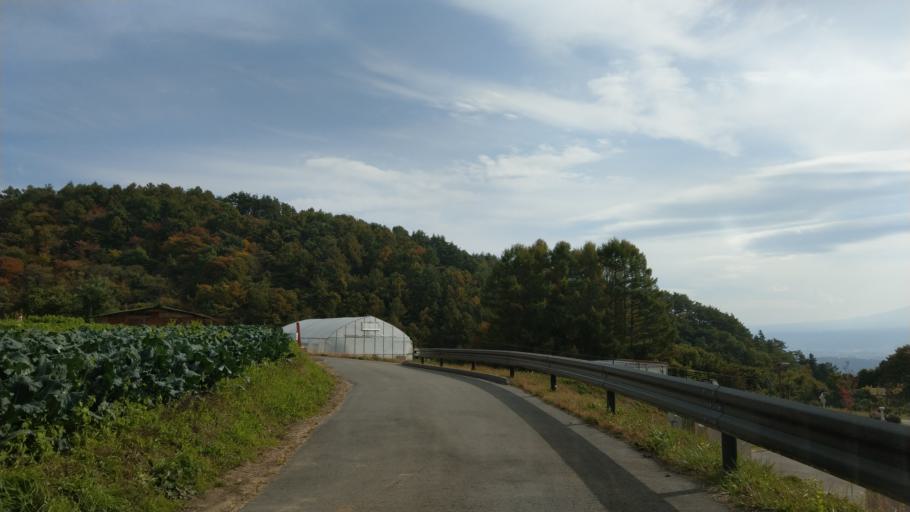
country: JP
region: Nagano
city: Komoro
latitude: 36.3493
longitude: 138.4367
